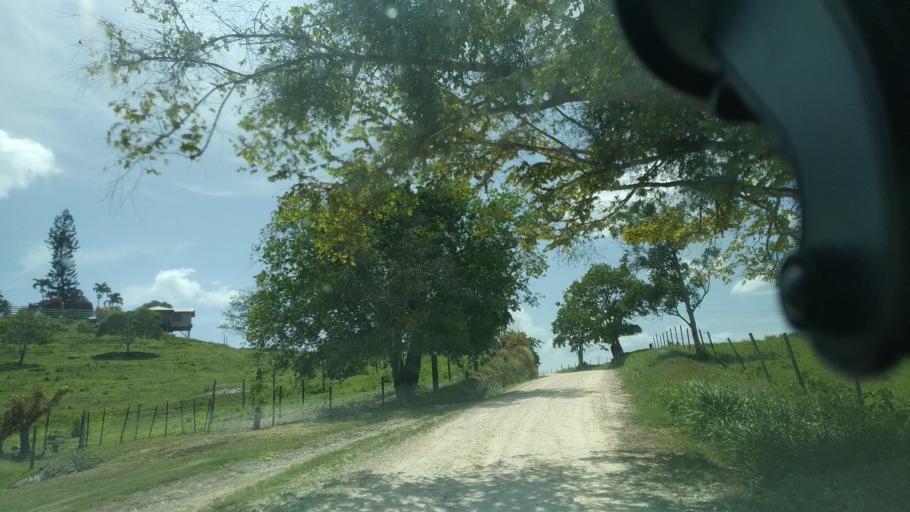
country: BZ
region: Cayo
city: San Ignacio
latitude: 17.3001
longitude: -89.0535
